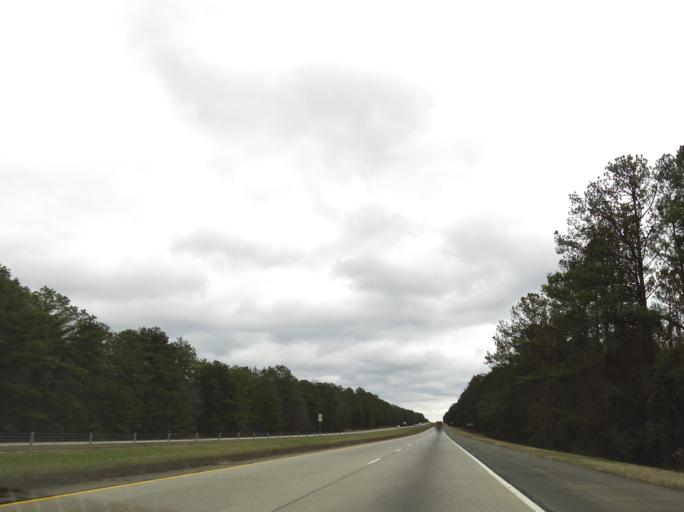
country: US
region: Georgia
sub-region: Houston County
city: Warner Robins
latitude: 32.7118
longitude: -83.5218
